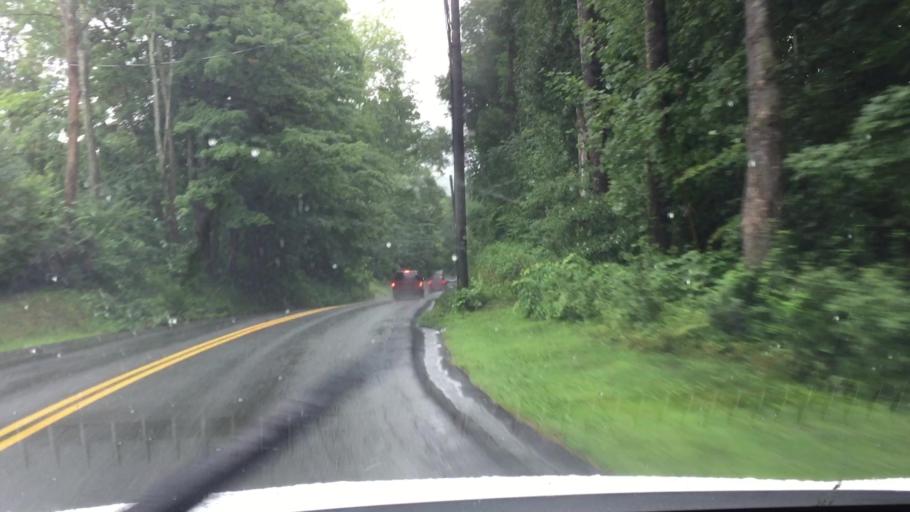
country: US
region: Massachusetts
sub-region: Berkshire County
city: Lanesborough
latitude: 42.5453
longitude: -73.2388
